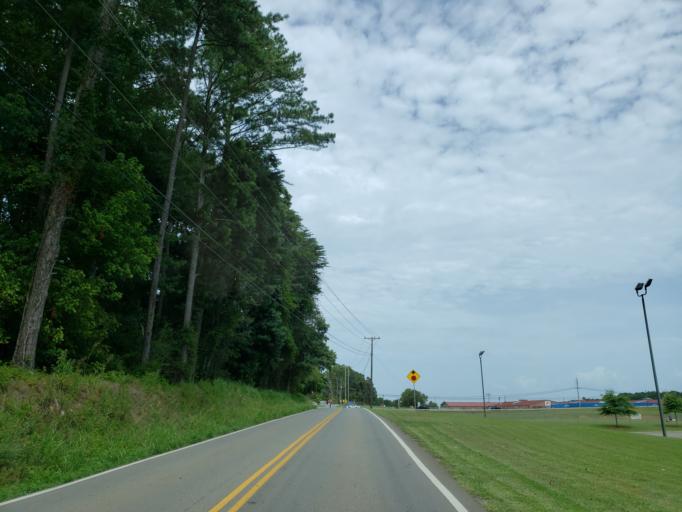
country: US
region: Georgia
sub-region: Pickens County
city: Jasper
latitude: 34.4458
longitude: -84.4239
